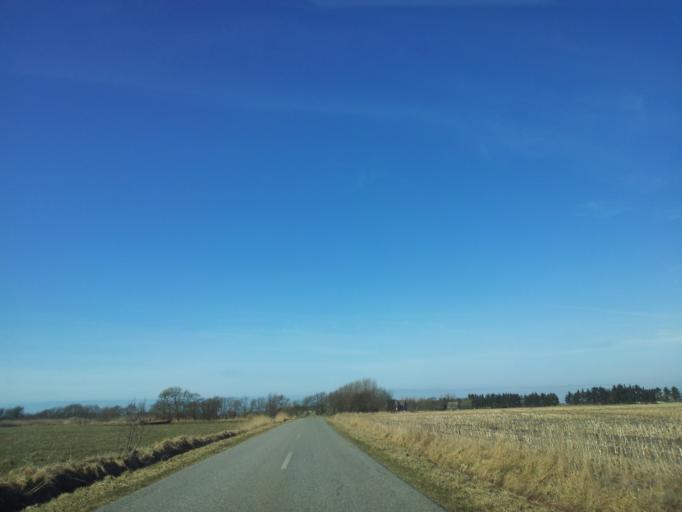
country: DK
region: South Denmark
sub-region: Tonder Kommune
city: Sherrebek
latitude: 55.1764
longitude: 8.7203
